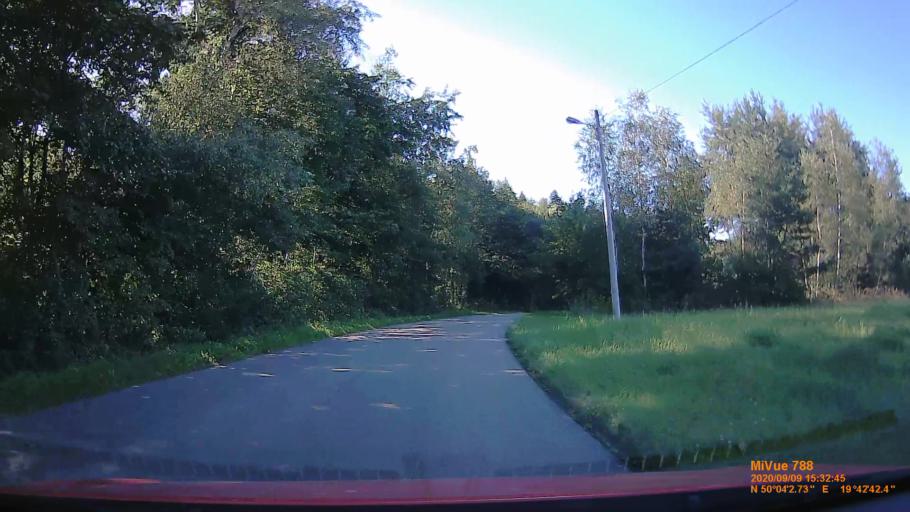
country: PL
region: Lesser Poland Voivodeship
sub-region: Powiat krakowski
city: Czulow
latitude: 50.0674
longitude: 19.7118
